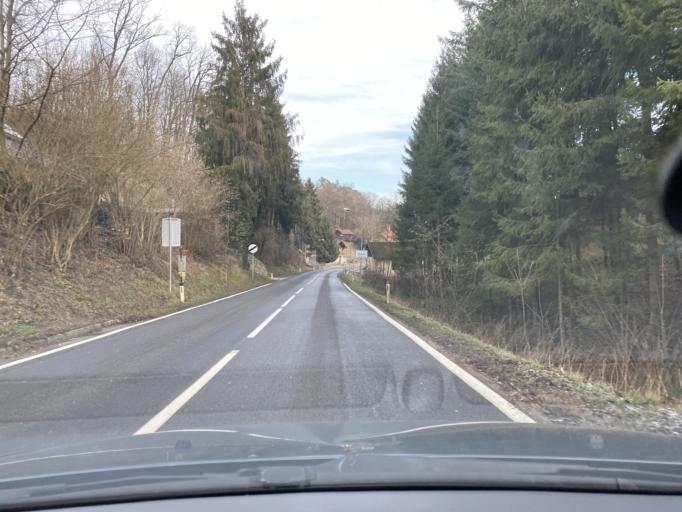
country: AT
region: Lower Austria
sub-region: Politischer Bezirk Melk
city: Loosdorf
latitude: 48.1703
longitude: 15.3701
